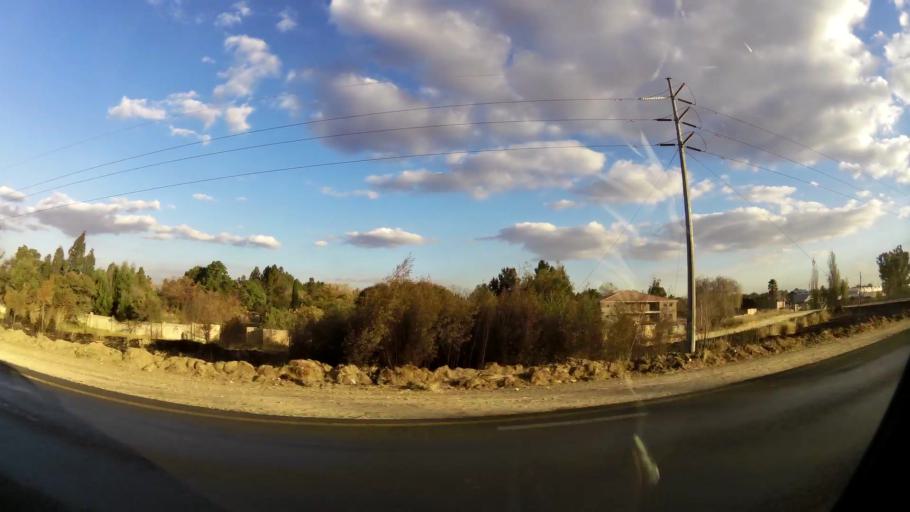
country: ZA
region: Gauteng
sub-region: City of Johannesburg Metropolitan Municipality
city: Midrand
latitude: -25.9476
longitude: 28.1665
